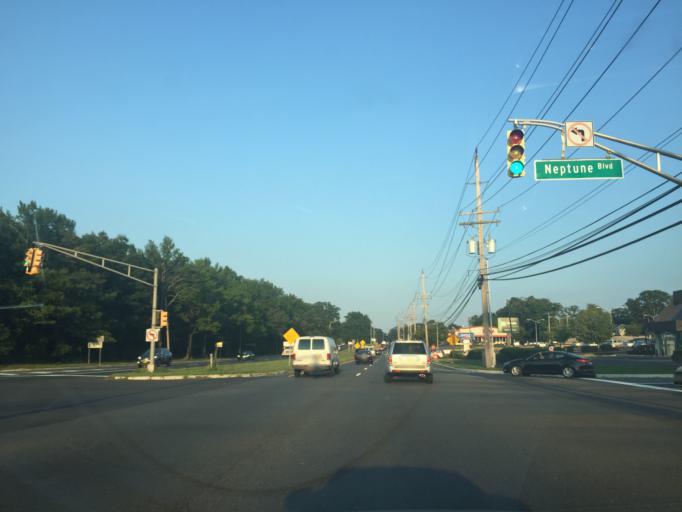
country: US
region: New Jersey
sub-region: Monmouth County
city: Wanamassa
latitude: 40.2272
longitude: -74.0438
